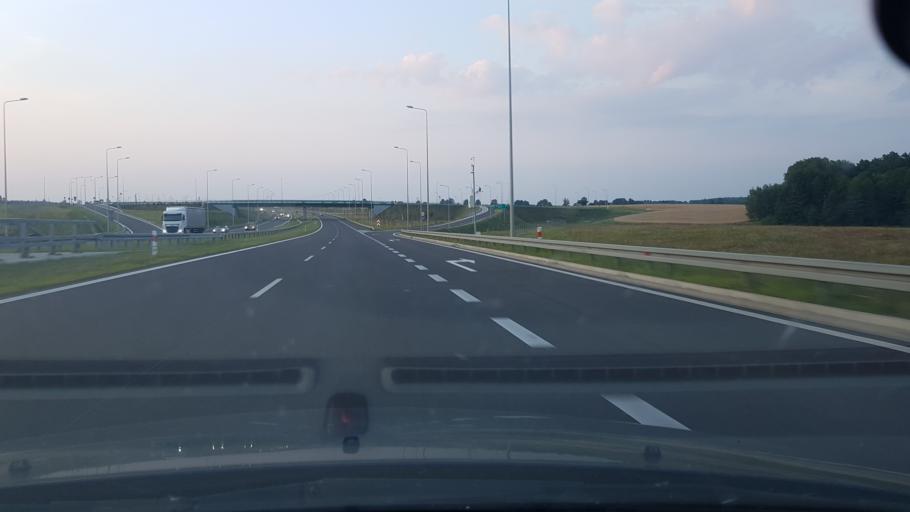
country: PL
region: Warmian-Masurian Voivodeship
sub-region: Powiat nidzicki
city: Nidzica
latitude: 53.2740
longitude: 20.4358
